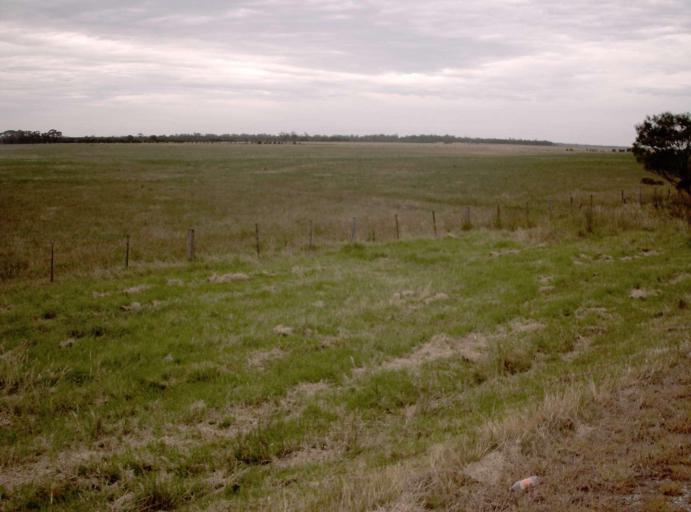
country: AU
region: Victoria
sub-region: Wellington
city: Sale
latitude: -38.2010
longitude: 147.3162
